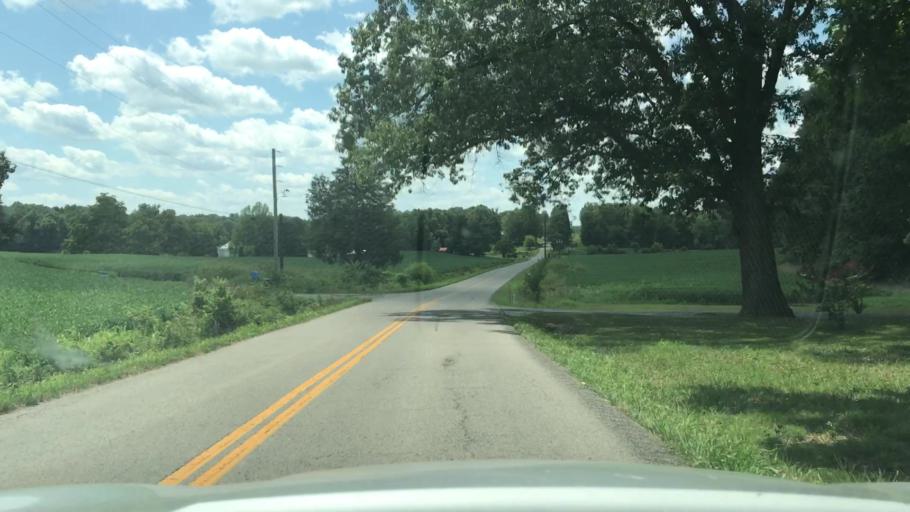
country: US
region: Kentucky
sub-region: Muhlenberg County
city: Greenville
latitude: 37.1357
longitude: -87.2698
